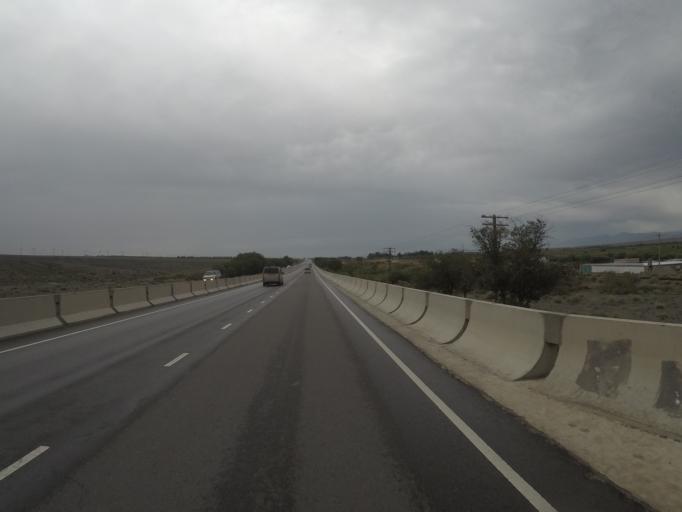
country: KG
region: Ysyk-Koel
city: Balykchy
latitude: 42.4589
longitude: 76.0899
